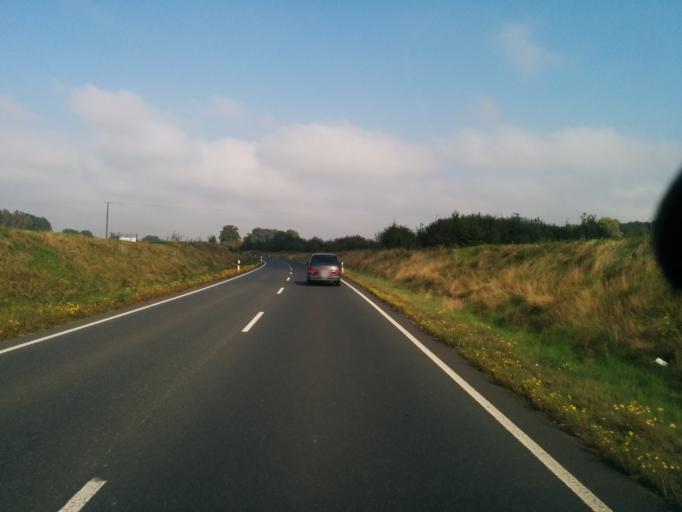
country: DE
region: North Rhine-Westphalia
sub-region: Regierungsbezirk Munster
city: Coesfeld
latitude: 51.9046
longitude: 7.1954
